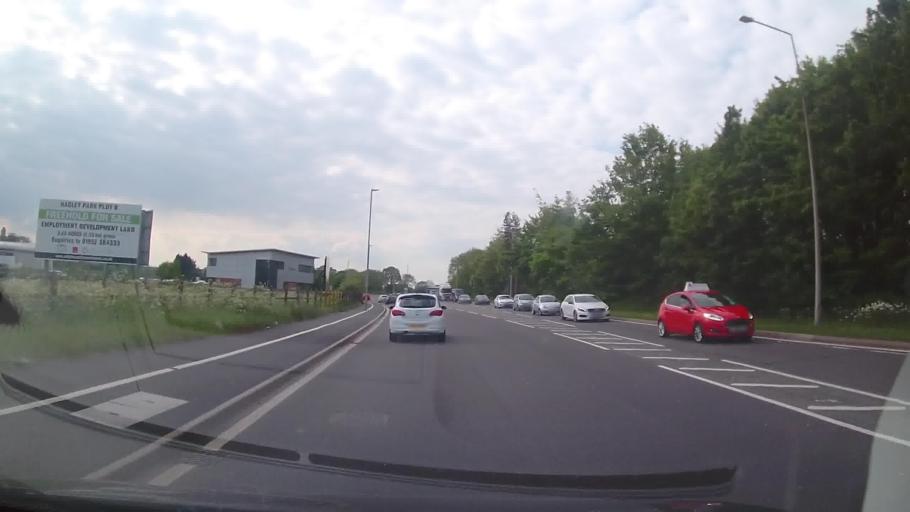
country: GB
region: England
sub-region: Shropshire
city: Hadley
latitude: 52.7186
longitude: -2.4755
